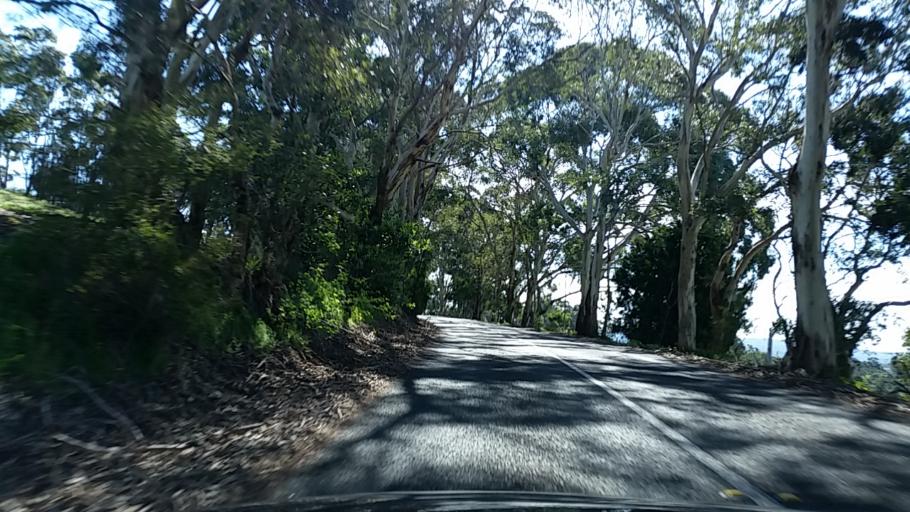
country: AU
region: South Australia
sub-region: Mount Barker
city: Little Hampton
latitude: -35.0758
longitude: 138.8183
